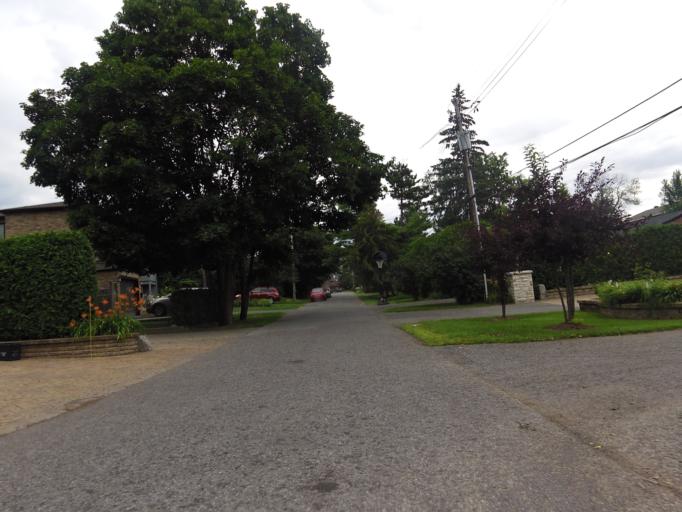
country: CA
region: Ontario
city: Bells Corners
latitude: 45.3557
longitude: -75.8469
